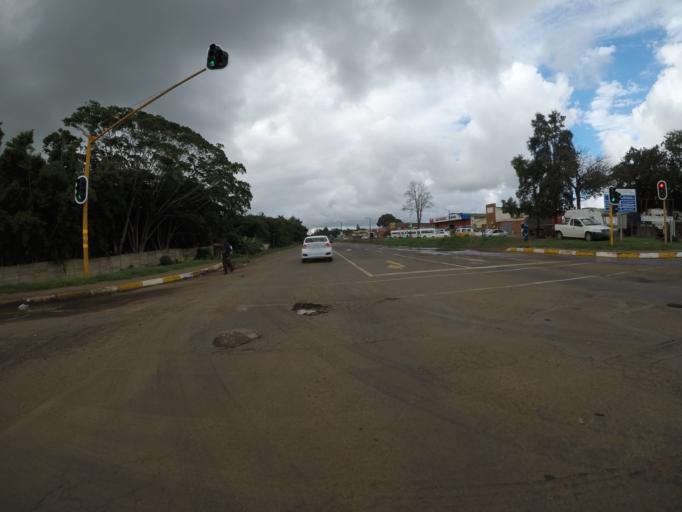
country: ZA
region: KwaZulu-Natal
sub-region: uMkhanyakude District Municipality
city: Mtubatuba
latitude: -28.4142
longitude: 32.1840
